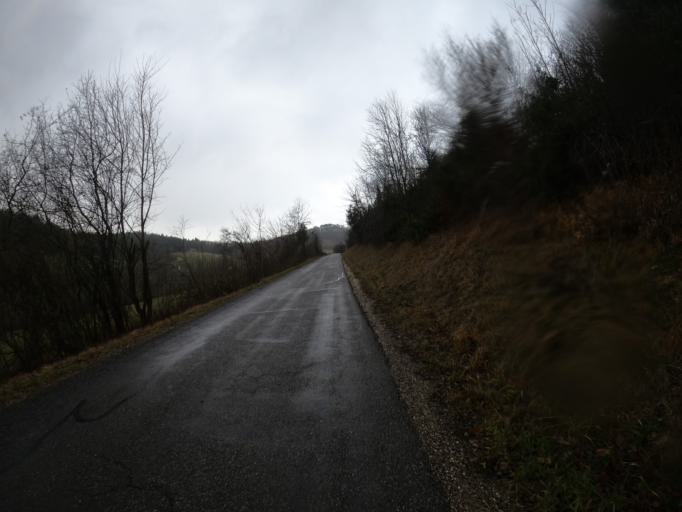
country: DE
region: Baden-Wuerttemberg
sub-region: Regierungsbezirk Stuttgart
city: Waldstetten
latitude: 48.7251
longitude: 9.8438
